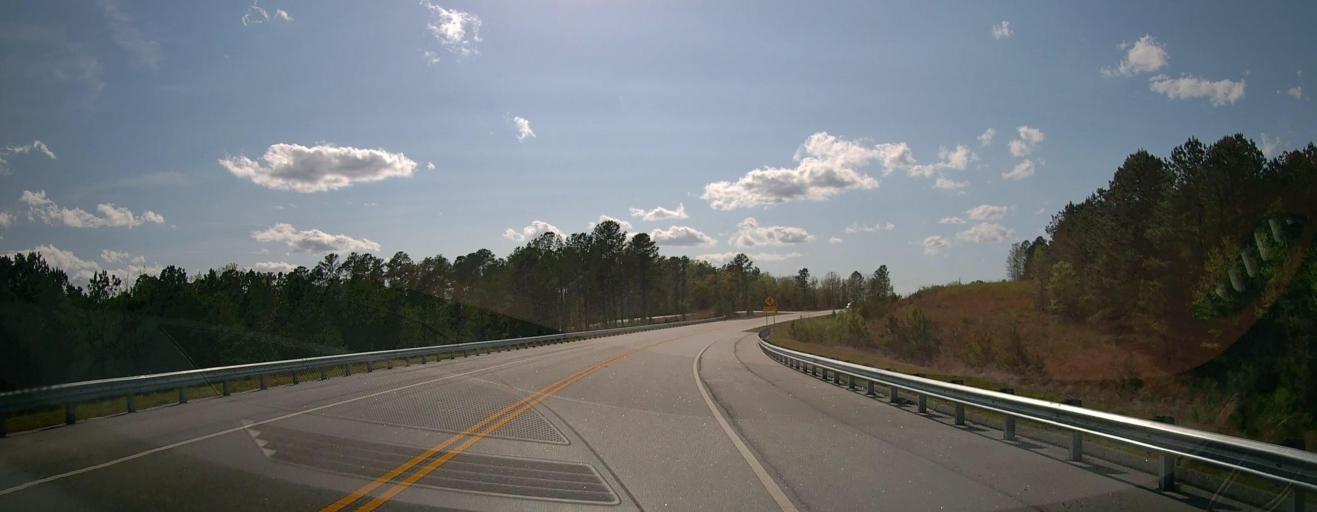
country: US
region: Georgia
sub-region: Baldwin County
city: Hardwick
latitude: 33.0175
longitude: -83.1033
